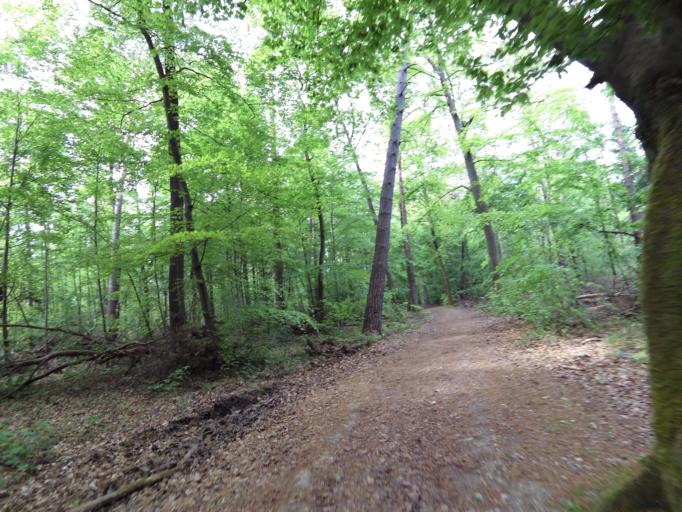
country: DE
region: North Rhine-Westphalia
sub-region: Regierungsbezirk Koln
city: Bonn
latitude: 50.6880
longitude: 7.1044
